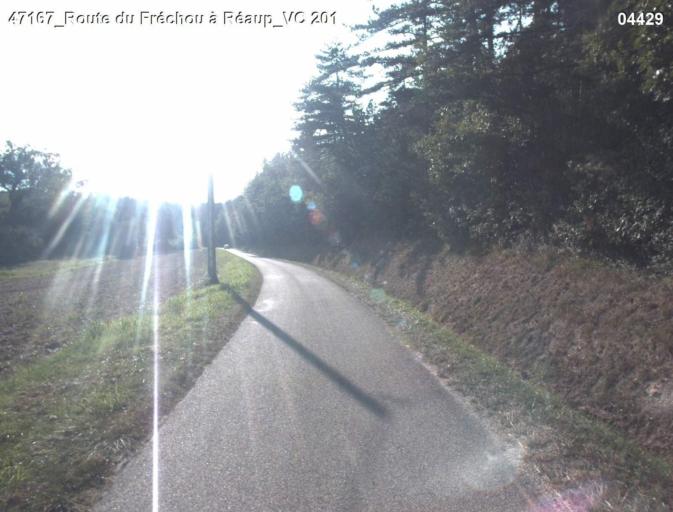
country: FR
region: Aquitaine
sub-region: Departement du Lot-et-Garonne
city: Mezin
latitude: 44.0736
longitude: 0.2631
